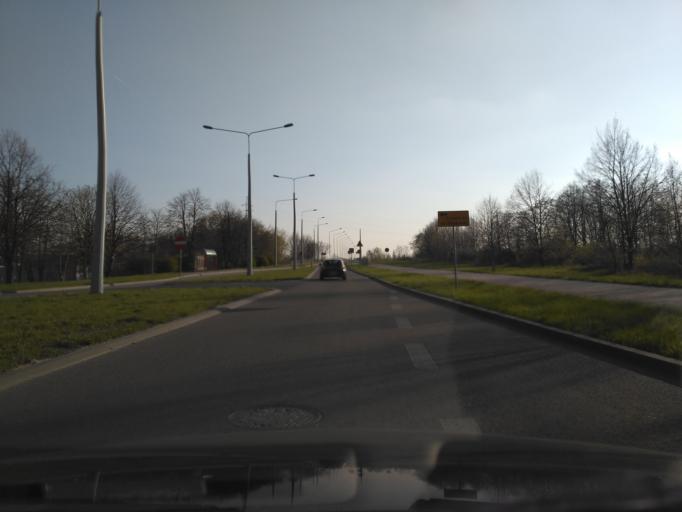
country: PL
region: Lublin Voivodeship
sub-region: Powiat lubelski
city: Jakubowice Murowane
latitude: 51.2412
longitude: 22.6345
